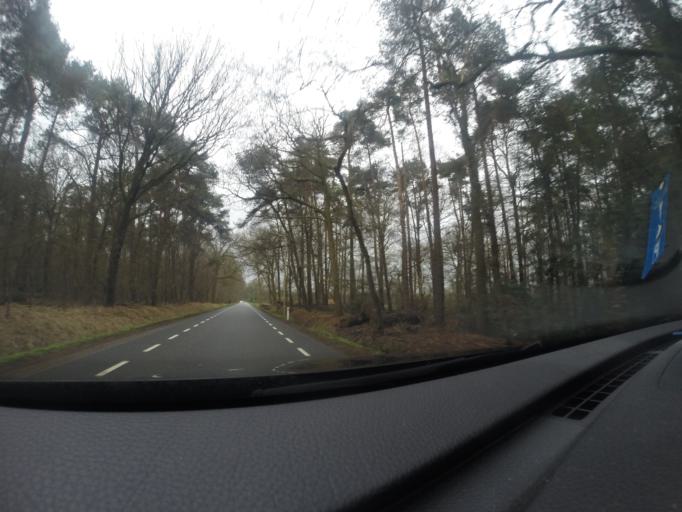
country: NL
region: Overijssel
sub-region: Gemeente Hof van Twente
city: Delden
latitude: 52.2350
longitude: 6.7302
